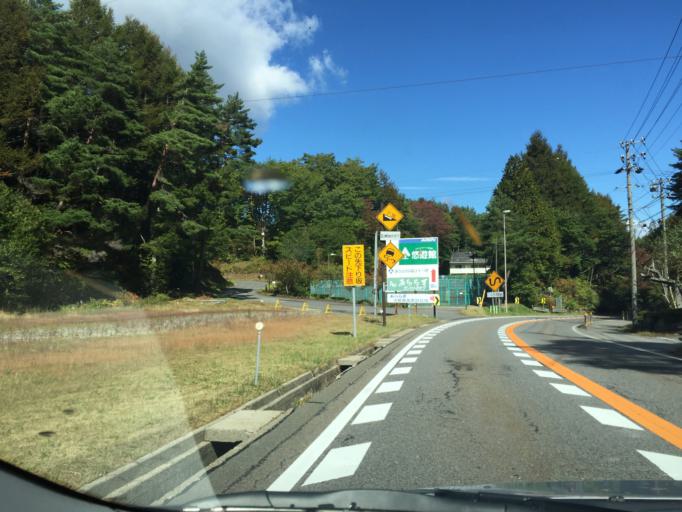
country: JP
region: Gifu
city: Nakatsugawa
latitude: 35.3588
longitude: 137.6720
